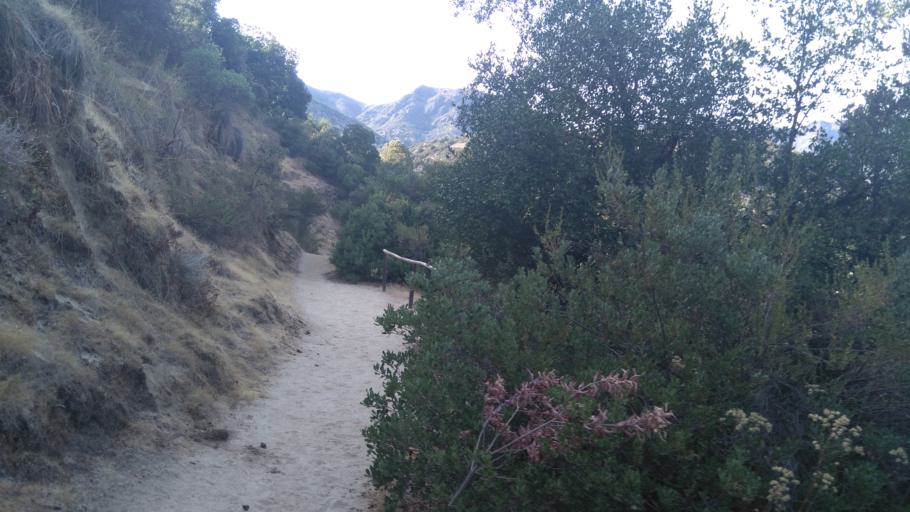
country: CL
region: Santiago Metropolitan
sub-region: Provincia de Cordillera
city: Puente Alto
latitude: -33.7259
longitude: -70.4744
